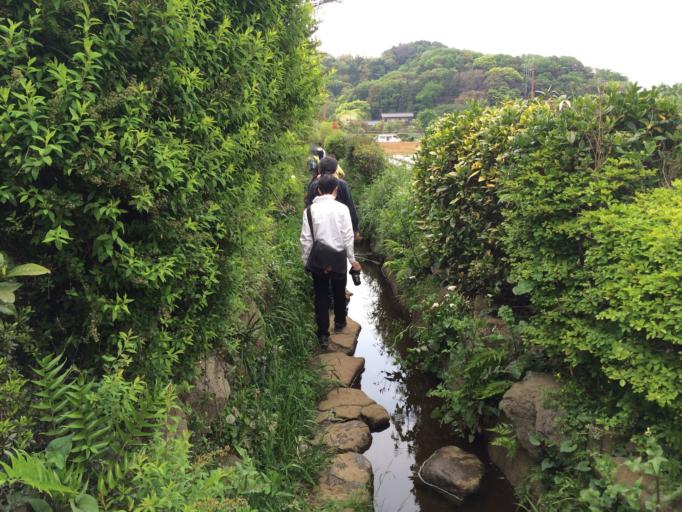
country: JP
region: Kanagawa
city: Yokohama
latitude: 35.5198
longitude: 139.6440
